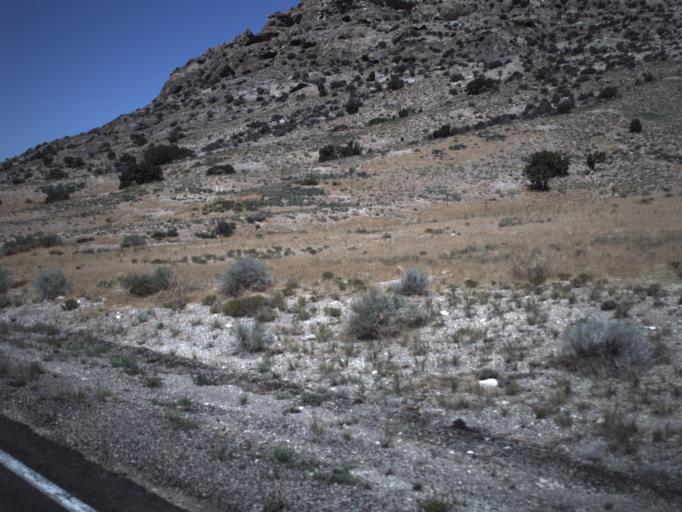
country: US
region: Utah
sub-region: Beaver County
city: Milford
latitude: 39.0717
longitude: -113.6498
